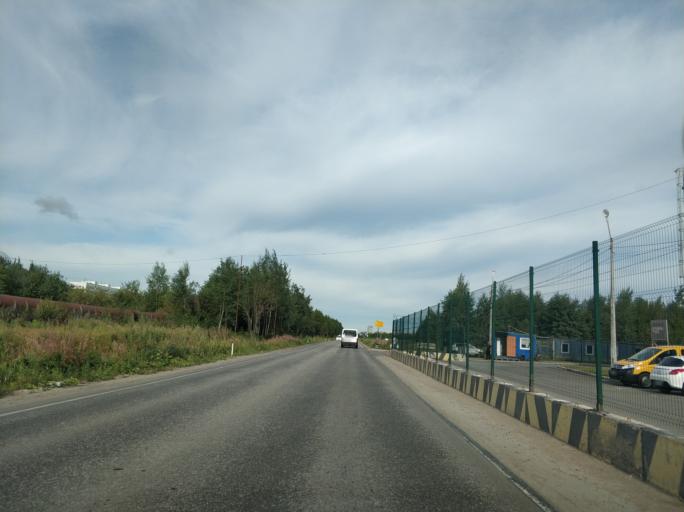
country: RU
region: St.-Petersburg
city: Grazhdanka
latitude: 60.0484
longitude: 30.4089
